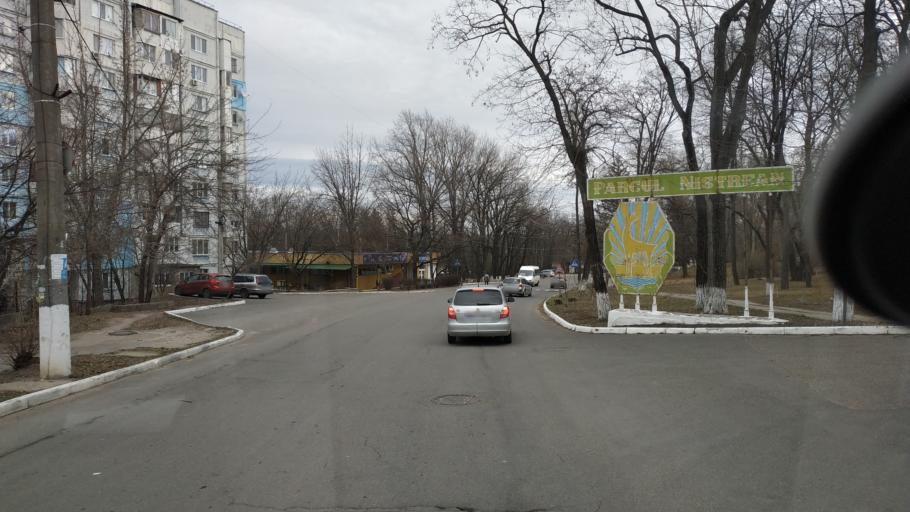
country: MD
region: Chisinau
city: Vadul lui Voda
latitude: 47.0864
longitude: 29.0845
